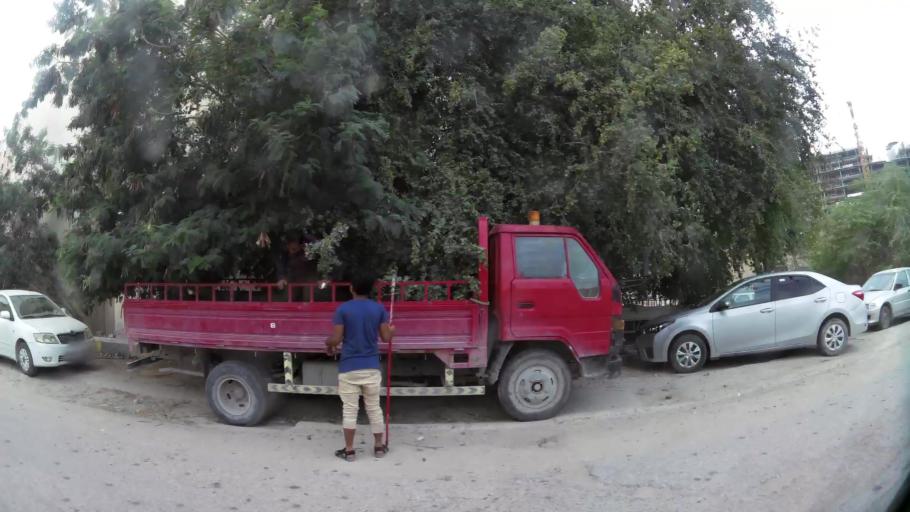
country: QA
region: Baladiyat ad Dawhah
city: Doha
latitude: 25.2830
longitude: 51.5201
